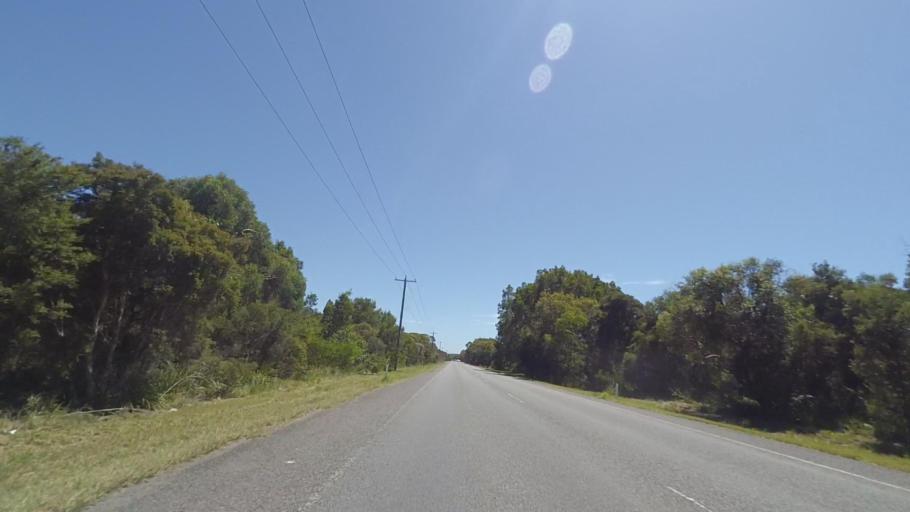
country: AU
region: New South Wales
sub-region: Port Stephens Shire
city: Medowie
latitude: -32.7901
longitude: 151.8545
